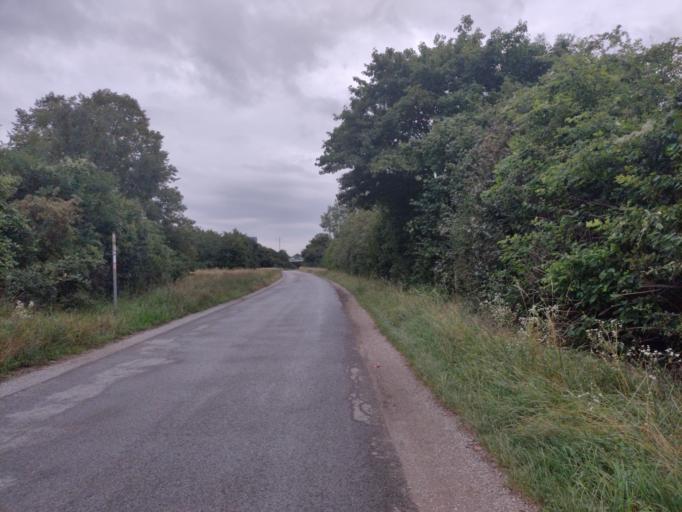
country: AT
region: Vienna
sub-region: Wien Stadt
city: Vienna
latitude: 48.2572
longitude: 16.3780
